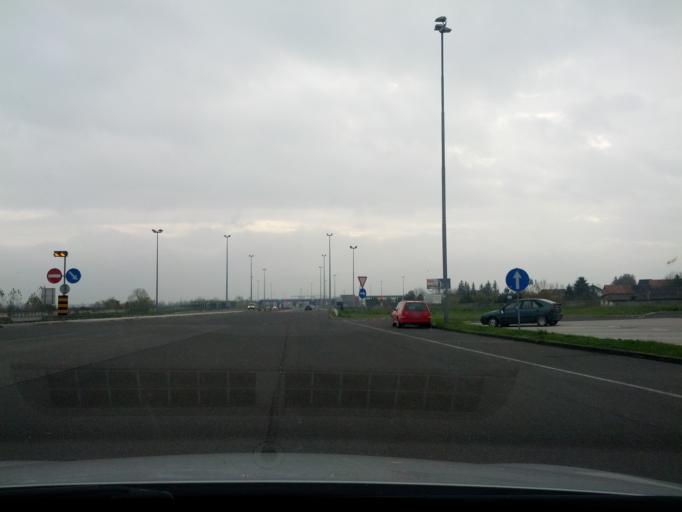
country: HR
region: Zagrebacka
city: Bregana
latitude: 45.8456
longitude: 15.6939
